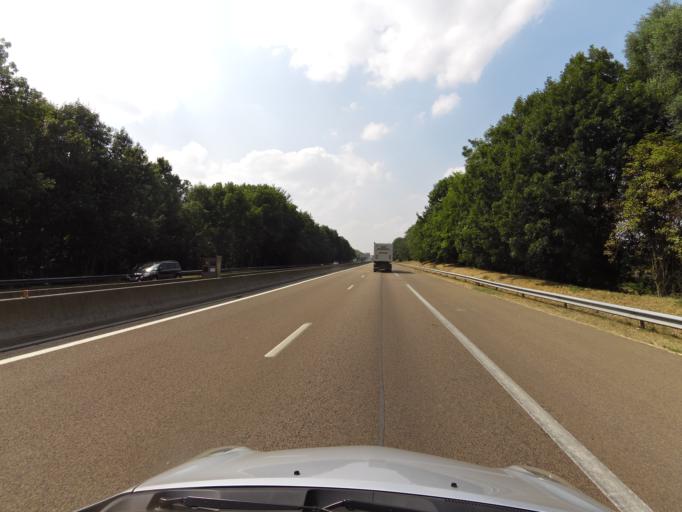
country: FR
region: Champagne-Ardenne
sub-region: Departement de la Marne
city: Tinqueux
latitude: 49.2548
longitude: 4.0027
